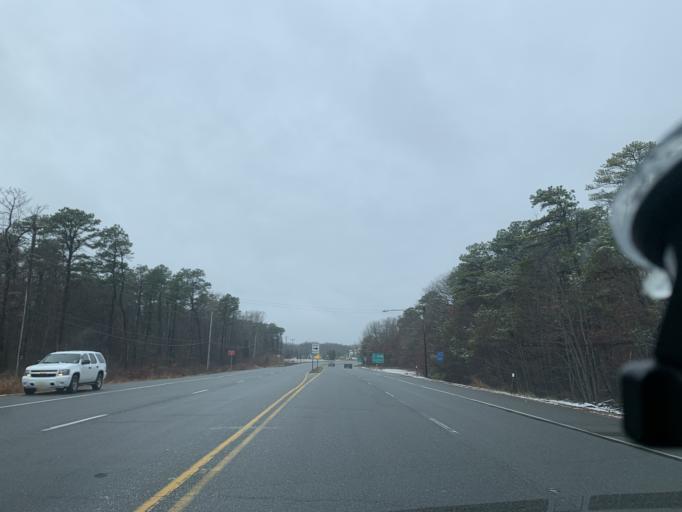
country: US
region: New Jersey
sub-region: Atlantic County
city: Pomona
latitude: 39.4498
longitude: -74.6337
